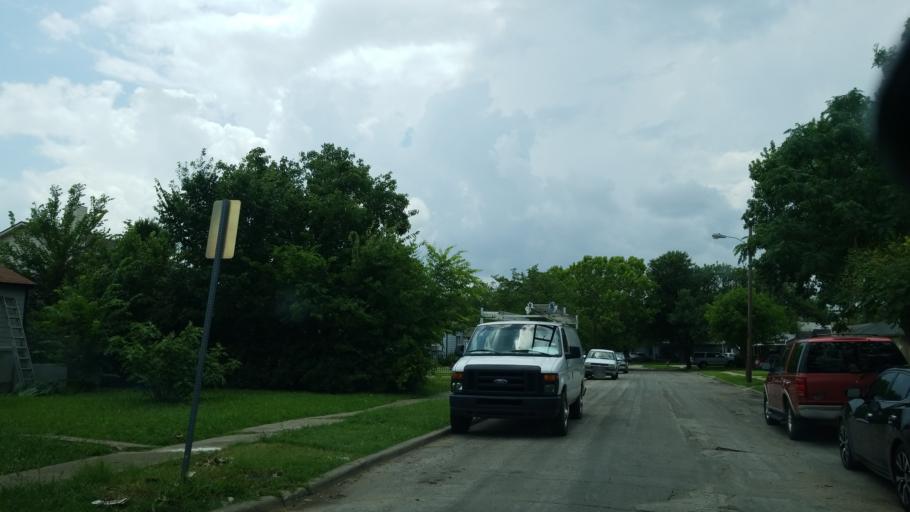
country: US
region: Texas
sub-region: Dallas County
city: University Park
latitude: 32.8768
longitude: -96.8564
